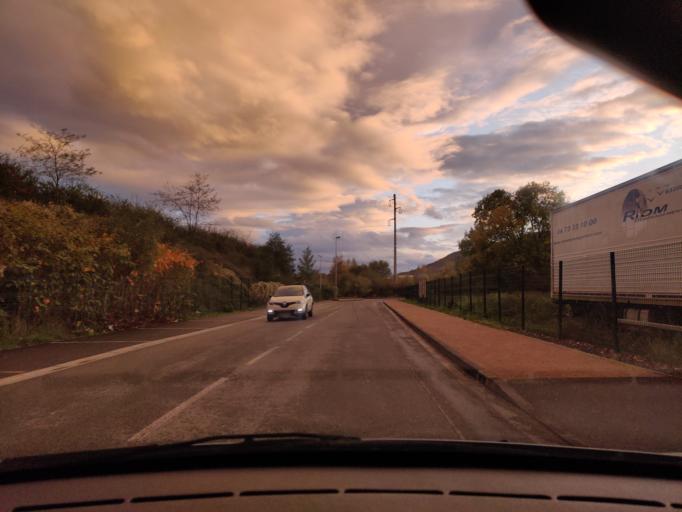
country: FR
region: Auvergne
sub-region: Departement du Puy-de-Dome
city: Menetrol
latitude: 45.8793
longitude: 3.1219
